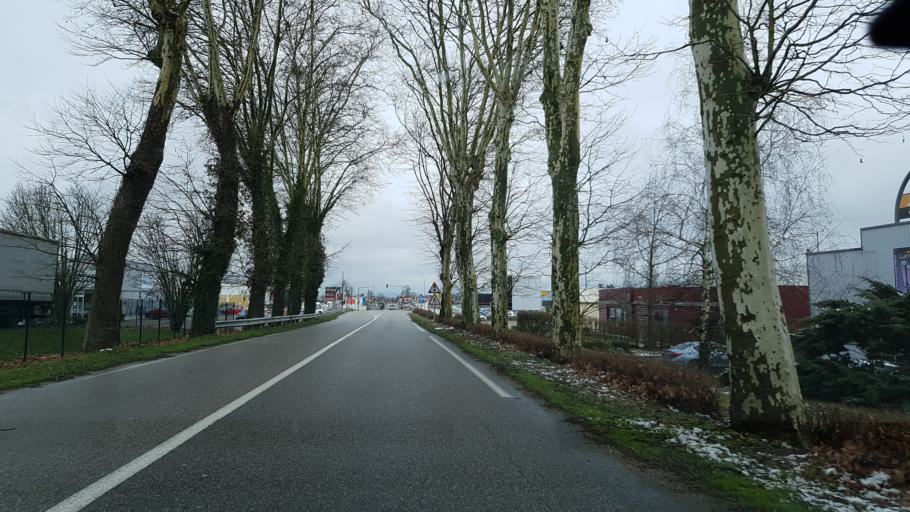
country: FR
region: Rhone-Alpes
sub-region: Departement de l'Ain
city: Peronnas
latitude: 46.1694
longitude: 5.1955
